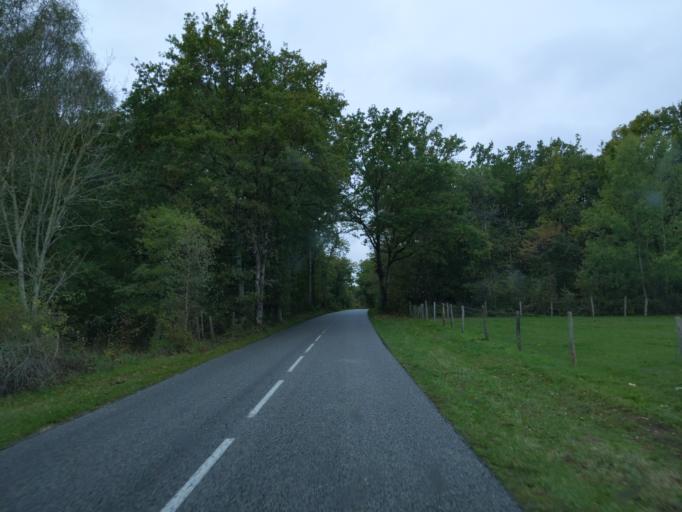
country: FR
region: Ile-de-France
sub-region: Departement des Yvelines
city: Bullion
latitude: 48.6266
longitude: 1.9739
